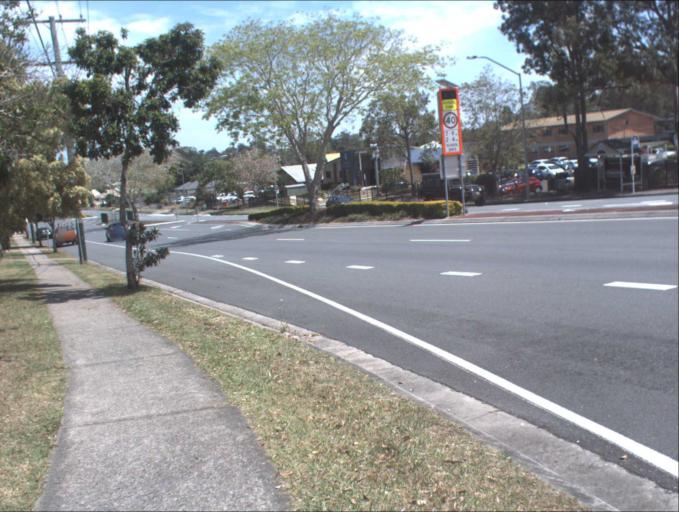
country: AU
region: Queensland
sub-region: Logan
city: Slacks Creek
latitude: -27.6353
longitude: 153.1482
